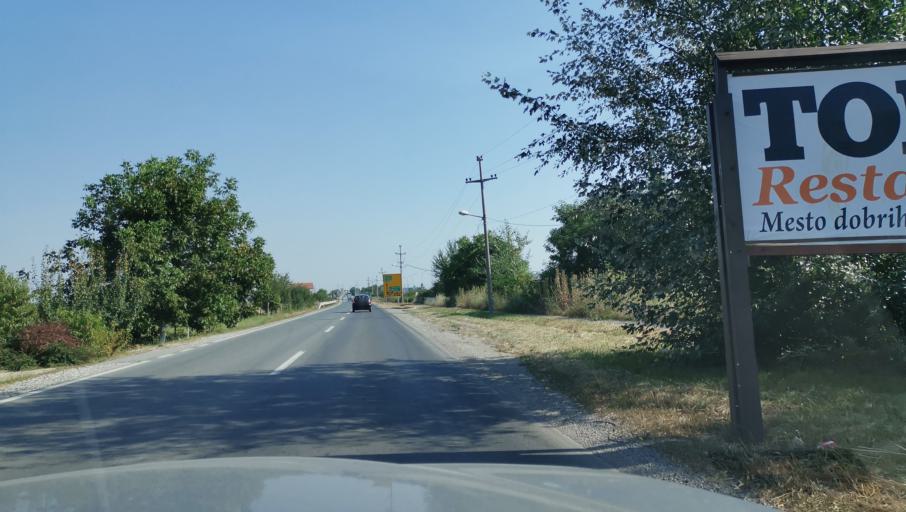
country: RS
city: Dobanovci
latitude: 44.8513
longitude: 20.2068
